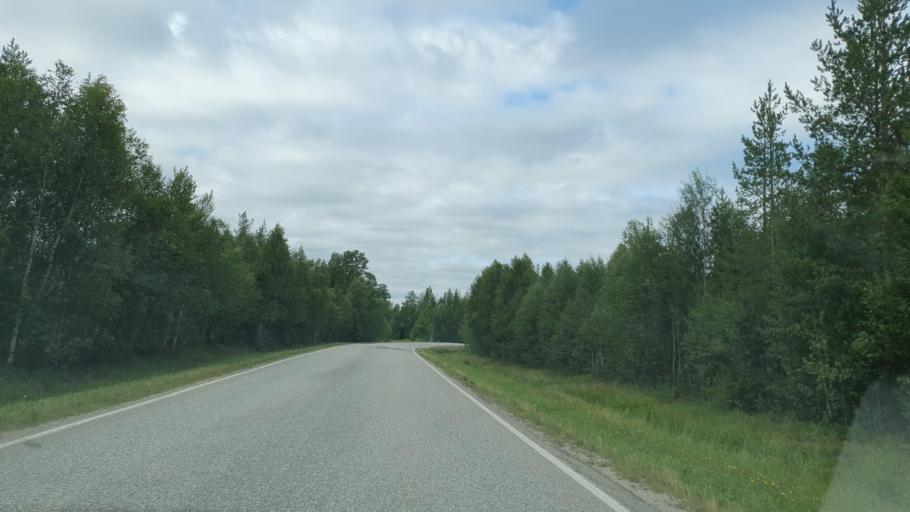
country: FI
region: Lapland
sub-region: Tunturi-Lappi
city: Kittilae
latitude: 67.6114
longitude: 25.2128
